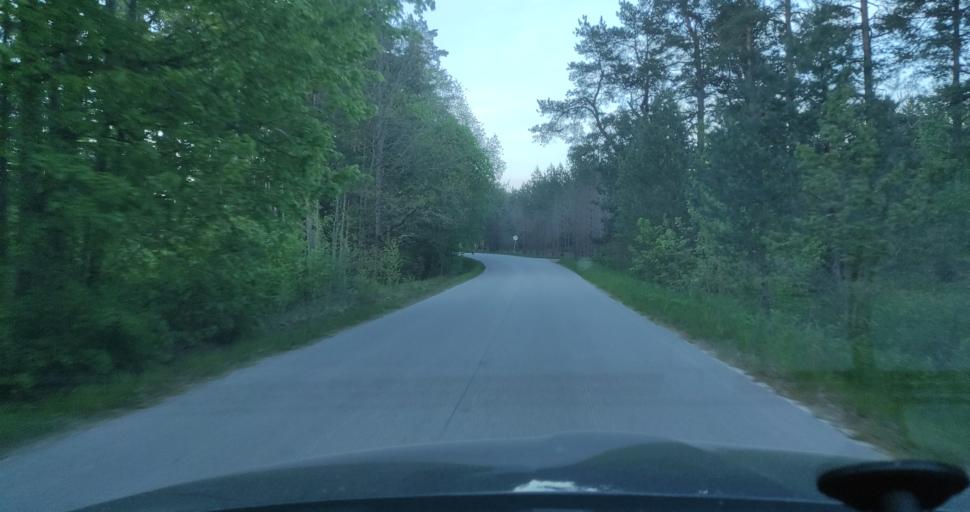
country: LV
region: Kuldigas Rajons
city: Kuldiga
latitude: 56.9555
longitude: 21.9380
